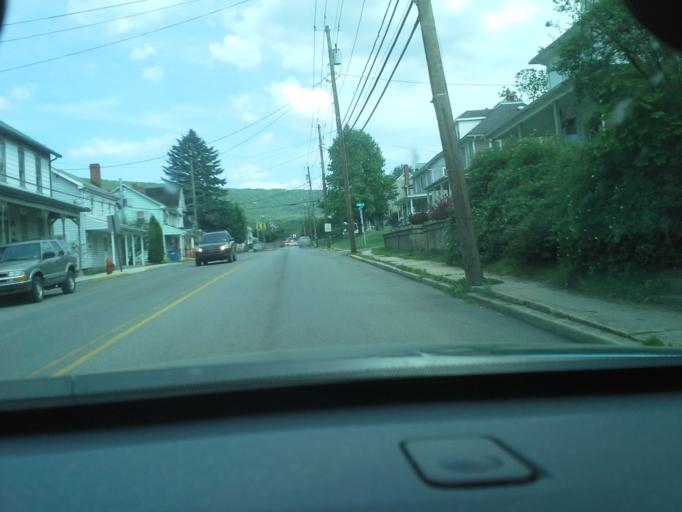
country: US
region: Pennsylvania
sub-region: Fulton County
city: McConnellsburg
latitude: 39.9309
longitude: -77.9943
